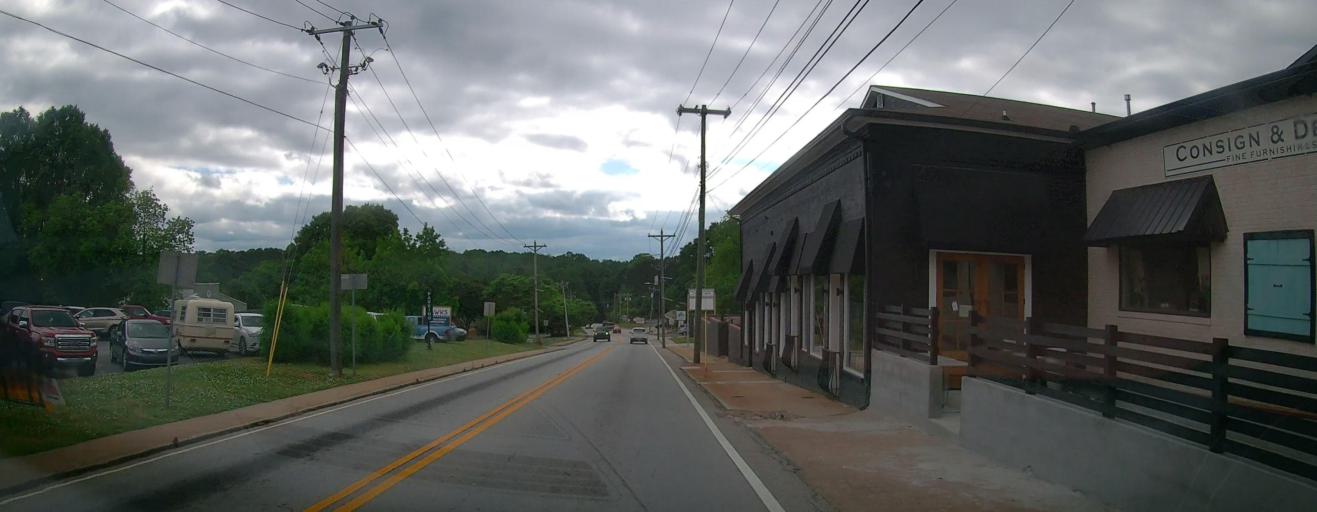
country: US
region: Georgia
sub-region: Walton County
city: Monroe
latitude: 33.7948
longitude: -83.7140
